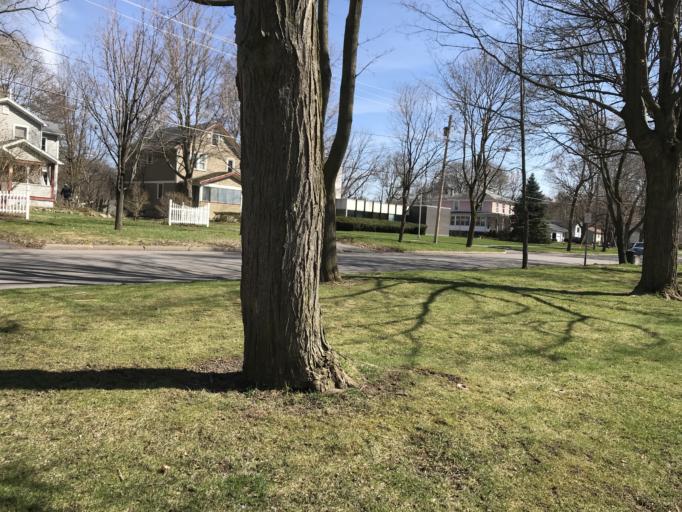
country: US
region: New York
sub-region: Livingston County
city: Geneseo
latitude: 42.7987
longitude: -77.8069
